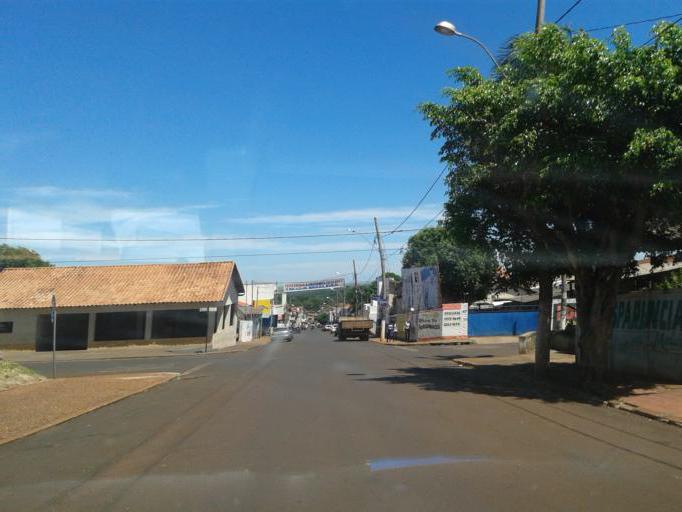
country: BR
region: Minas Gerais
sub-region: Capinopolis
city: Capinopolis
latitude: -18.6839
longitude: -49.5688
